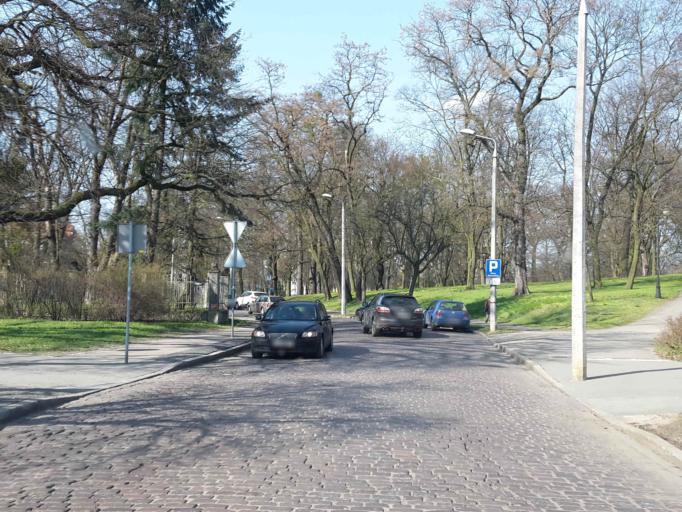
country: PL
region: Kujawsko-Pomorskie
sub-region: Torun
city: Torun
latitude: 53.0095
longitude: 18.5975
